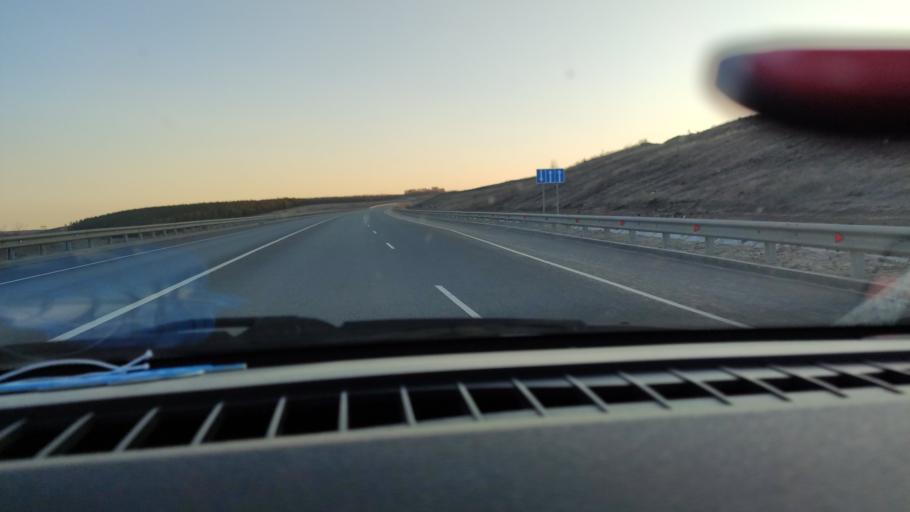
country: RU
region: Saratov
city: Yelshanka
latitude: 51.8746
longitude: 46.5056
